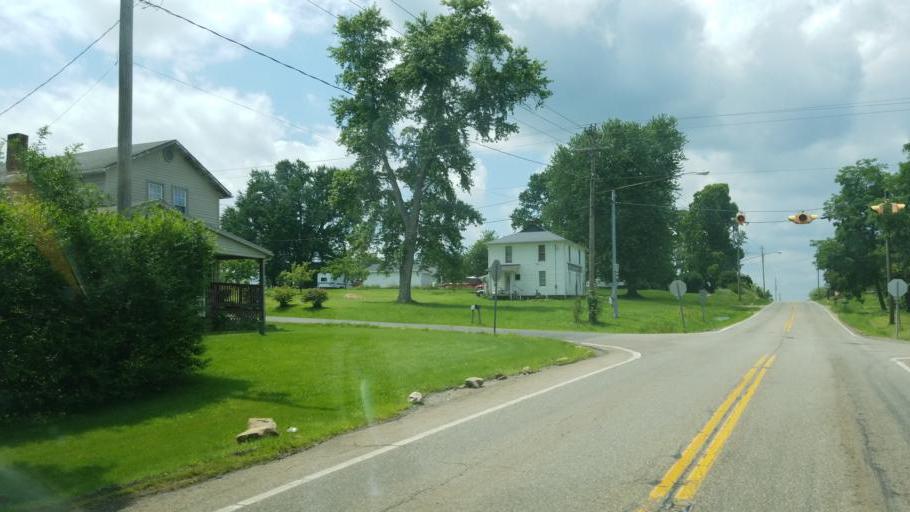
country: US
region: Ohio
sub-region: Stark County
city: Minerva
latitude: 40.7889
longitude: -80.9935
